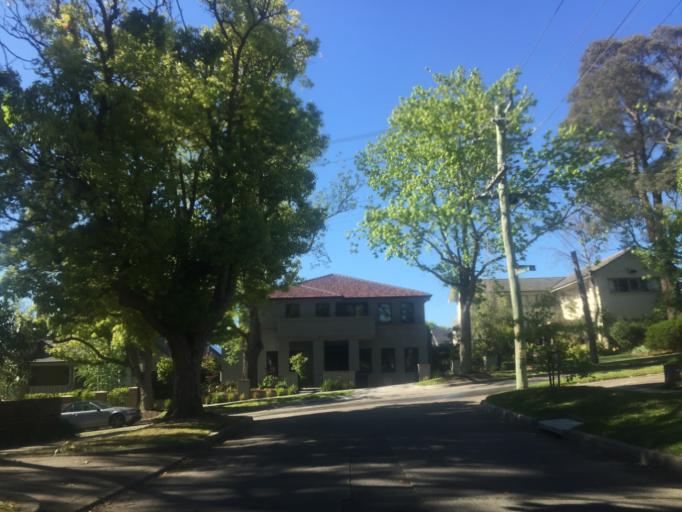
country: AU
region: Victoria
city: Balwyn
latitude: -37.8136
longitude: 145.0706
